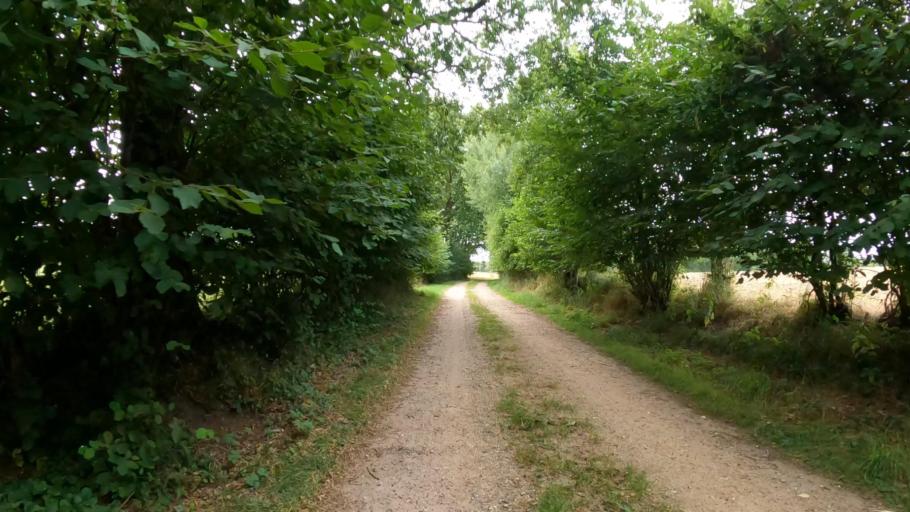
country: DE
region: Schleswig-Holstein
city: Seth
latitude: 53.8541
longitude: 10.2141
